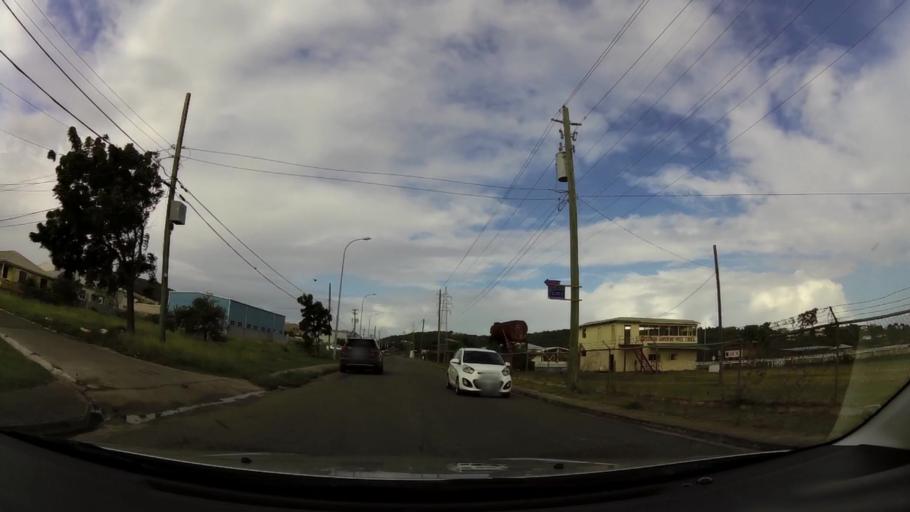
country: AG
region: Saint George
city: Piggotts
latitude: 17.1304
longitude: -61.8136
